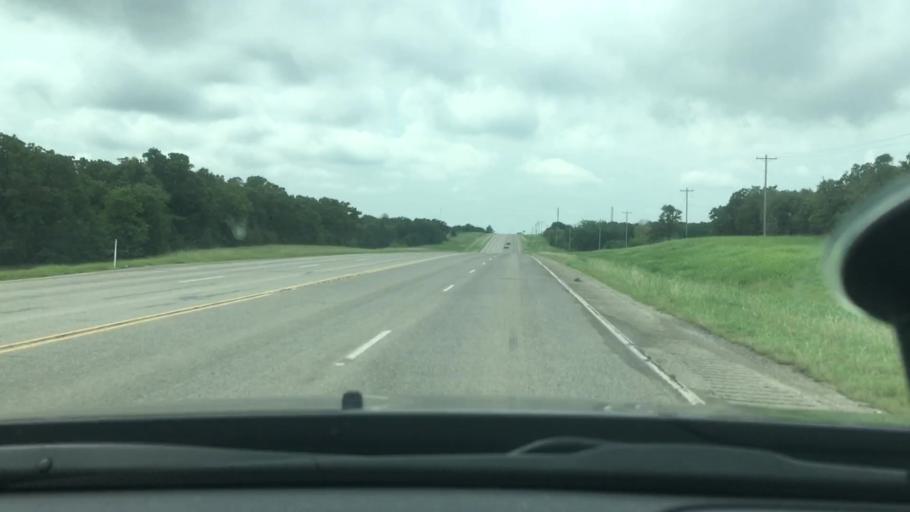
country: US
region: Oklahoma
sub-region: Carter County
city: Healdton
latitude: 34.1853
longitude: -97.4749
